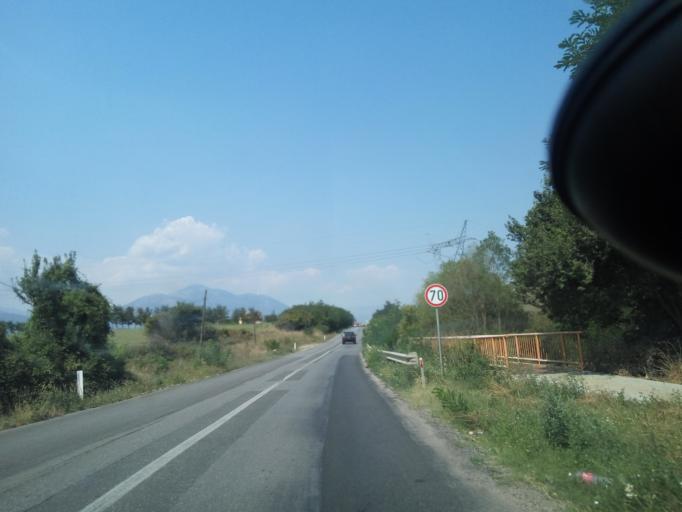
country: XK
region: Gjakova
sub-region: Komuna e Decanit
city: Gllogjan
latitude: 42.4639
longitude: 20.3476
